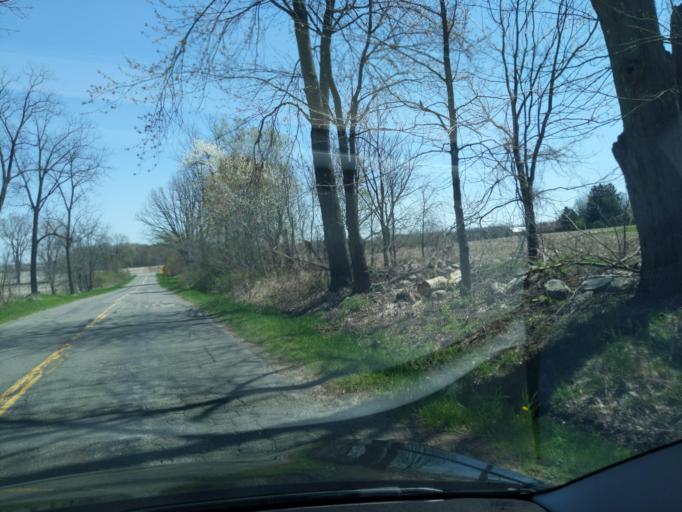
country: US
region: Michigan
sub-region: Ingham County
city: Mason
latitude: 42.5531
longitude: -84.5063
